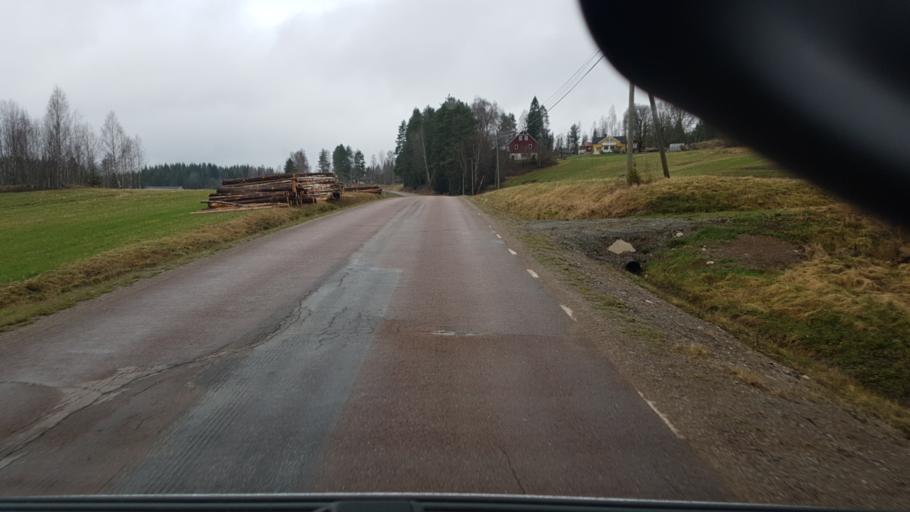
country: SE
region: Vaermland
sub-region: Eda Kommun
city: Amotfors
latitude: 59.9132
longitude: 12.5223
